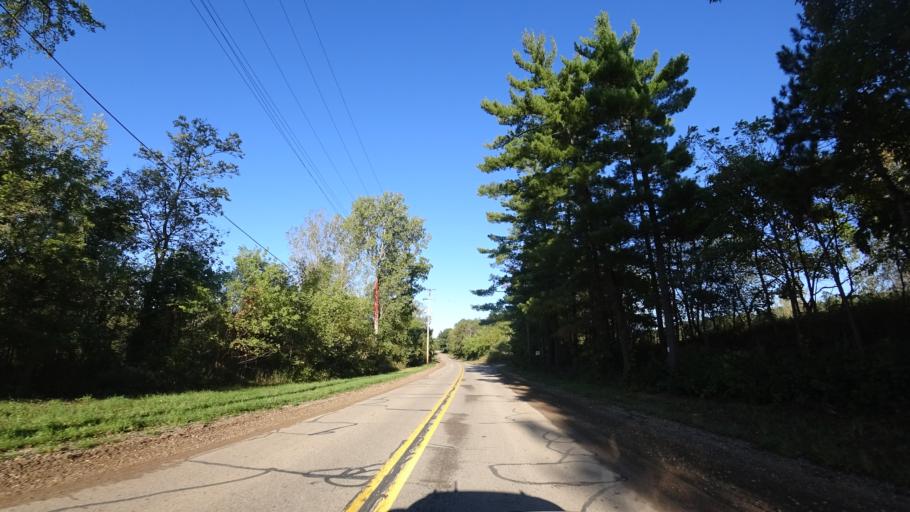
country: US
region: Michigan
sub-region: Kent County
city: Wyoming
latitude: 42.9460
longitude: -85.7316
